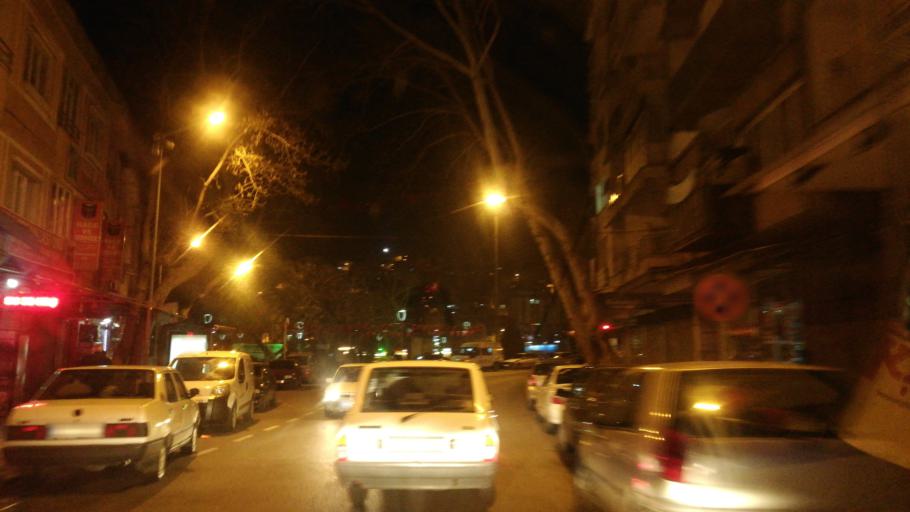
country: TR
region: Kahramanmaras
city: Kahramanmaras
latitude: 37.5857
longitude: 36.9276
